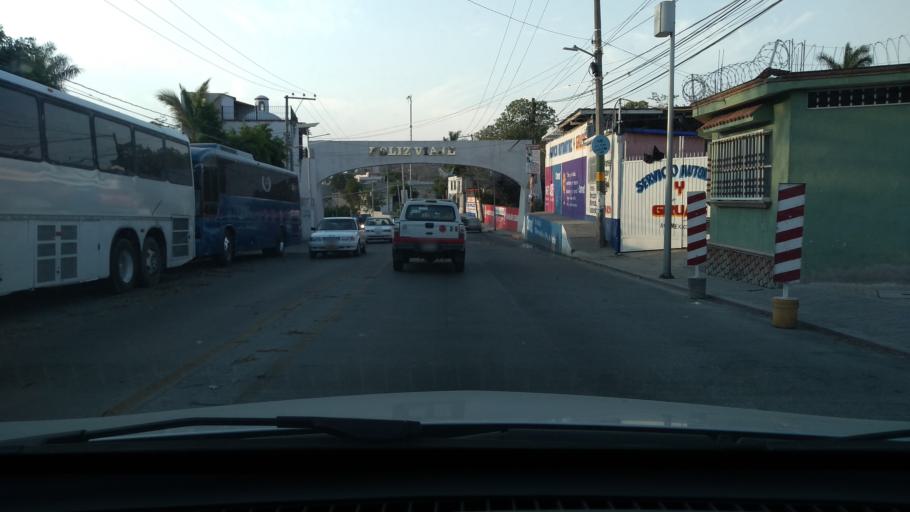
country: MX
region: Morelos
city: Puente de Ixtla
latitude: 18.6293
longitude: -99.3226
